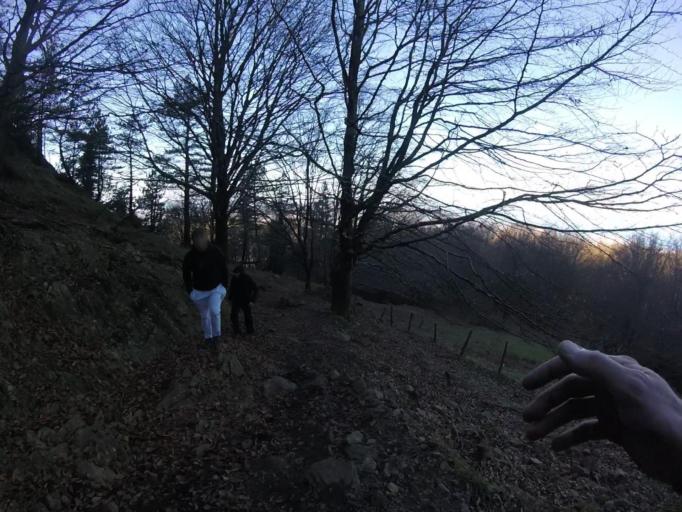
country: ES
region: Basque Country
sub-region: Provincia de Guipuzcoa
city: Irun
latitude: 43.2907
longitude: -1.7854
